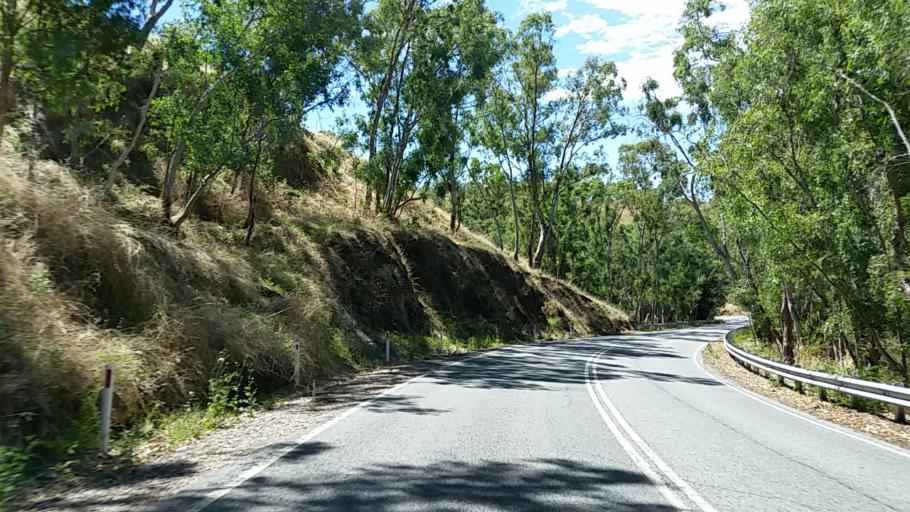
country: AU
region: South Australia
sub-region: Tea Tree Gully
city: Golden Grove
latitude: -34.8542
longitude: 138.7909
